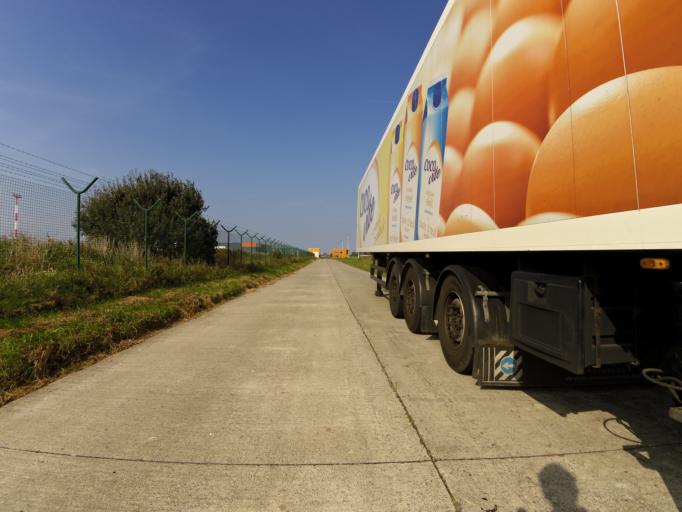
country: BE
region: Flanders
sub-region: Provincie West-Vlaanderen
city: Ostend
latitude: 51.1973
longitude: 2.8986
